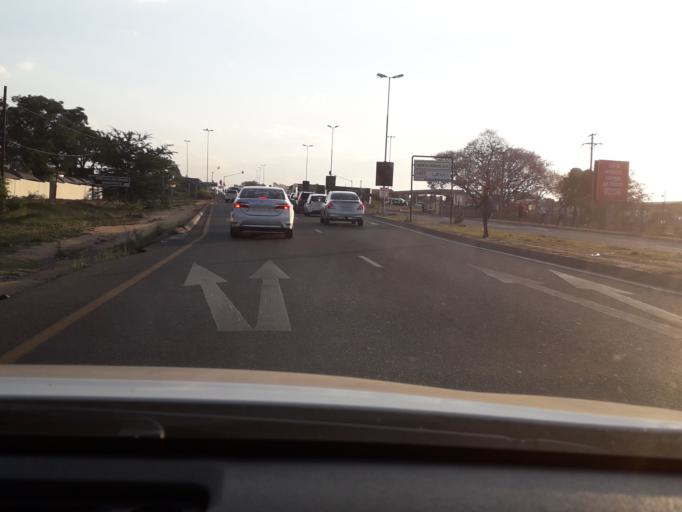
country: ZA
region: Gauteng
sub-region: West Rand District Municipality
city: Muldersdriseloop
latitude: -26.0424
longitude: 27.9565
